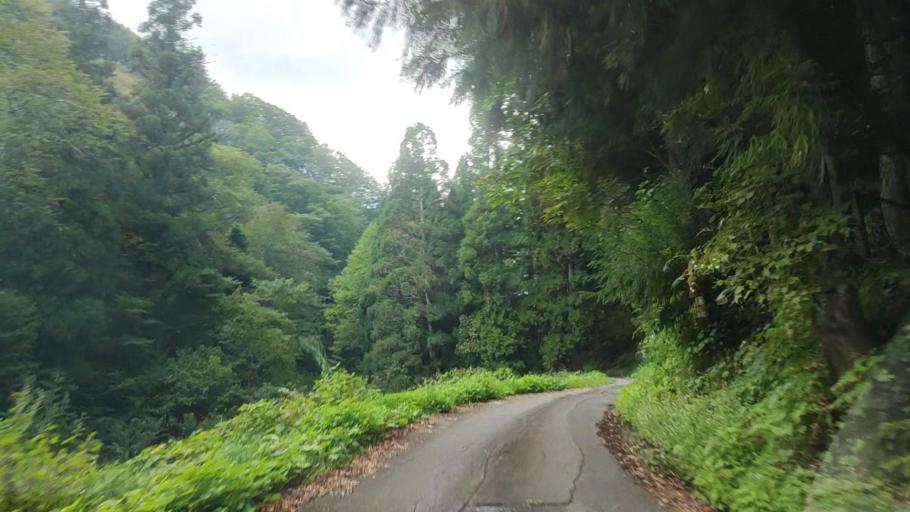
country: JP
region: Gifu
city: Takayama
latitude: 36.3174
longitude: 137.0840
